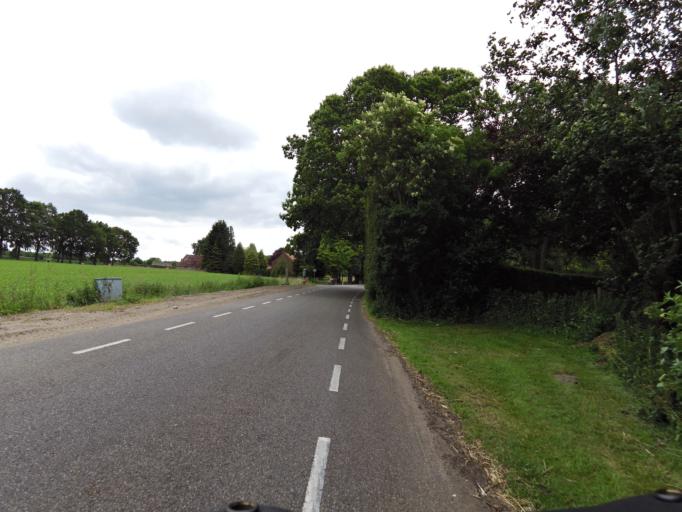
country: NL
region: North Brabant
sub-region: Gemeente Zundert
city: Zundert
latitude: 51.5053
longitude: 4.7323
